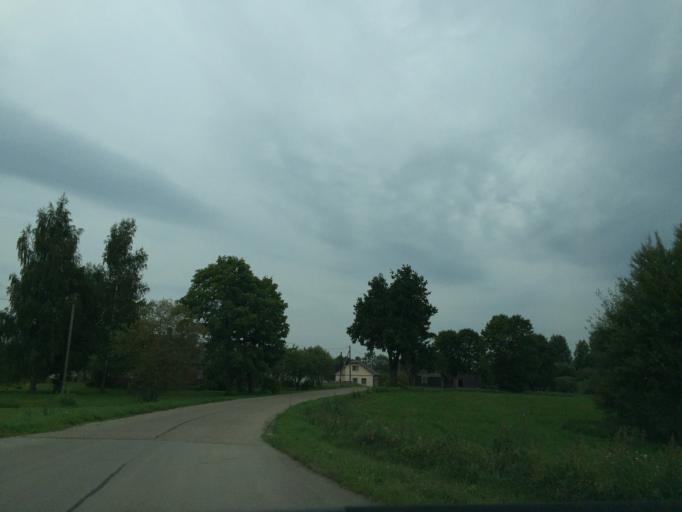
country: LV
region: Cibla
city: Cibla
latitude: 56.4056
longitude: 27.9370
